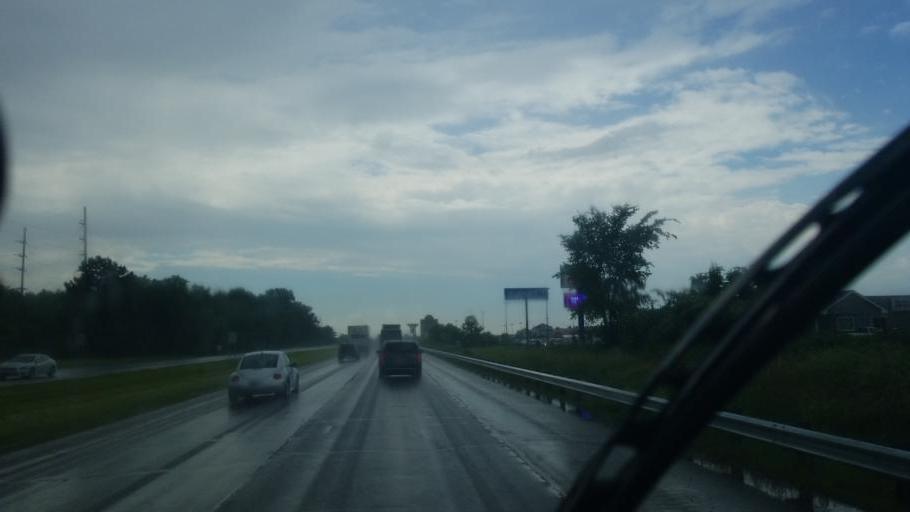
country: US
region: Indiana
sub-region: Whitley County
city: Columbia City
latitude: 41.1693
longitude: -85.4942
